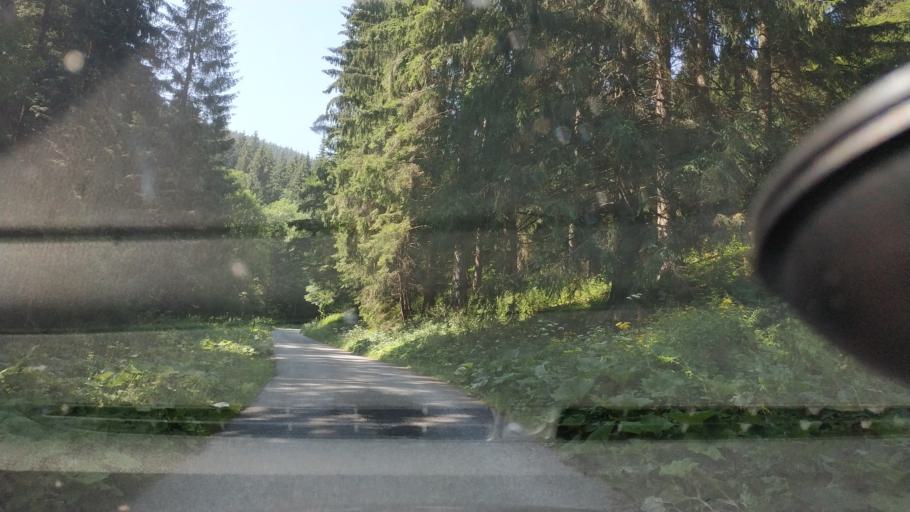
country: SK
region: Zilinsky
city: Ruzomberok
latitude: 48.9987
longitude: 19.2416
